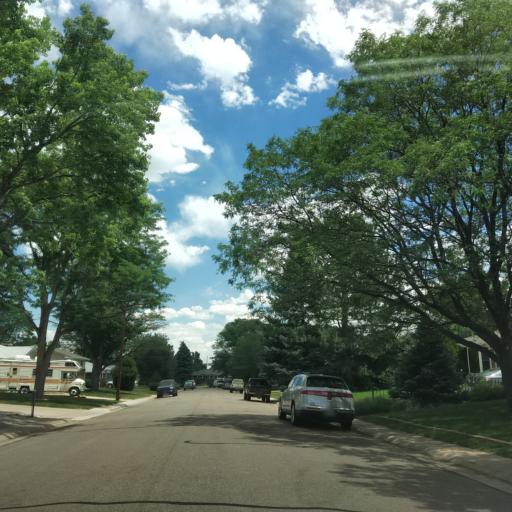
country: US
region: Colorado
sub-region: Jefferson County
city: Lakewood
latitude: 39.6887
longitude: -105.0844
